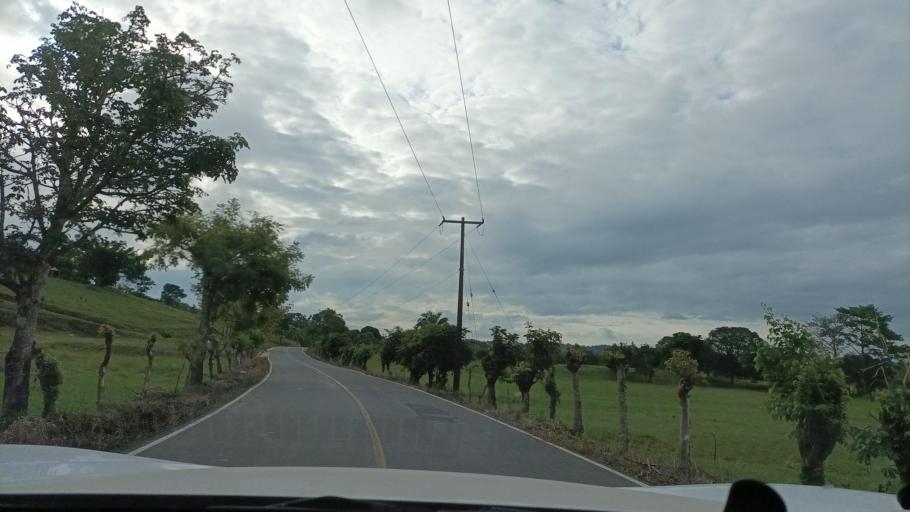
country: MX
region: Veracruz
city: Hidalgotitlan
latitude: 17.7436
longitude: -94.4917
